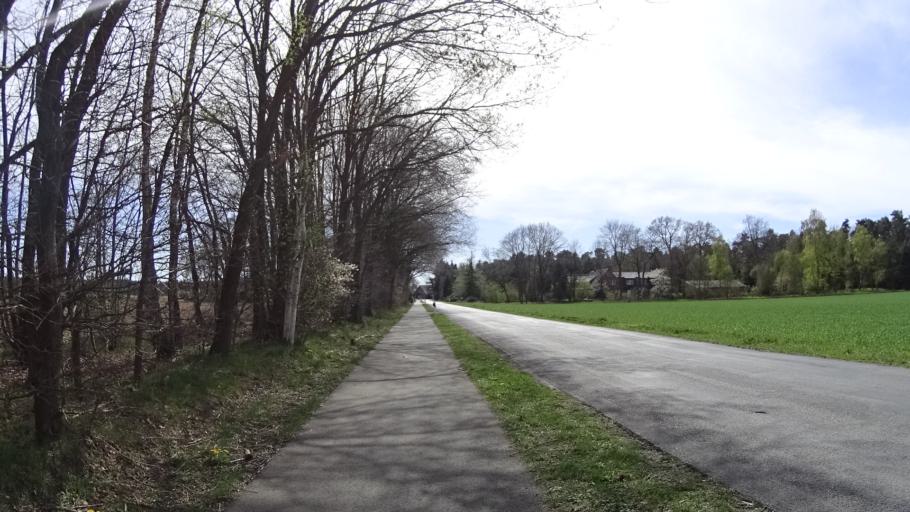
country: DE
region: Lower Saxony
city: Spelle
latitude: 52.3521
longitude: 7.4441
